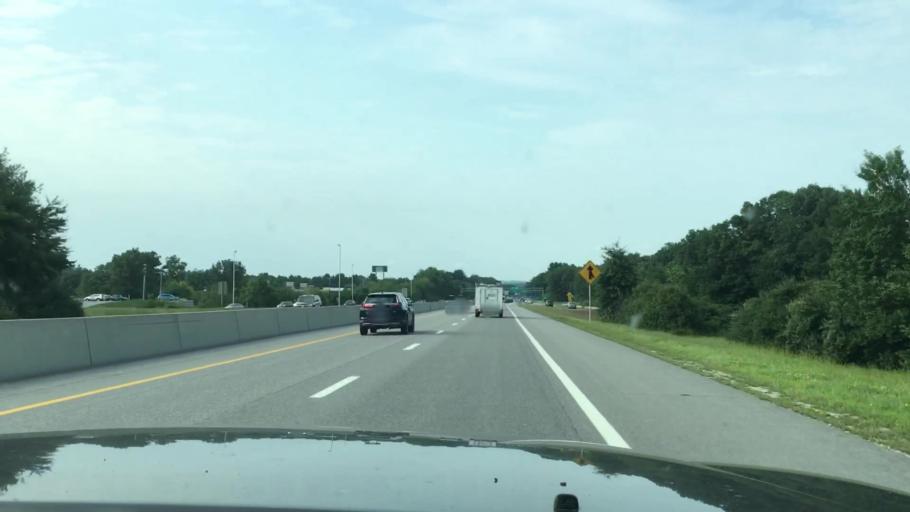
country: US
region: New Hampshire
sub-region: Hillsborough County
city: Bedford
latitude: 42.9526
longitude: -71.4729
